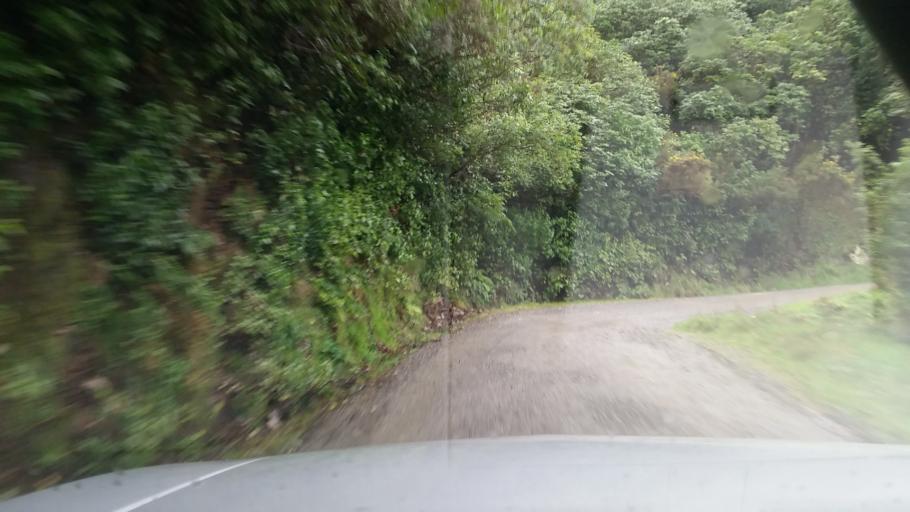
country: NZ
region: Marlborough
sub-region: Marlborough District
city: Picton
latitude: -41.1391
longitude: 174.0499
